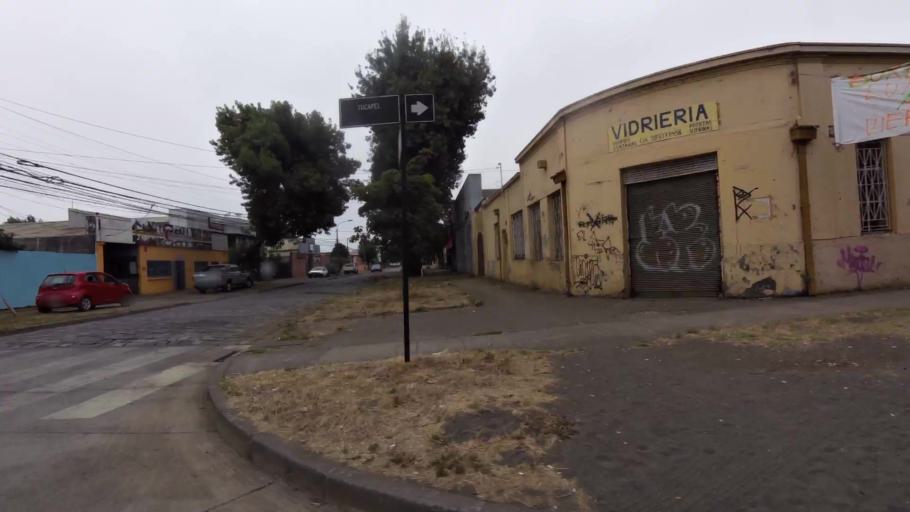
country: CL
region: Biobio
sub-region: Provincia de Concepcion
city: Concepcion
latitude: -36.8133
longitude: -73.0535
